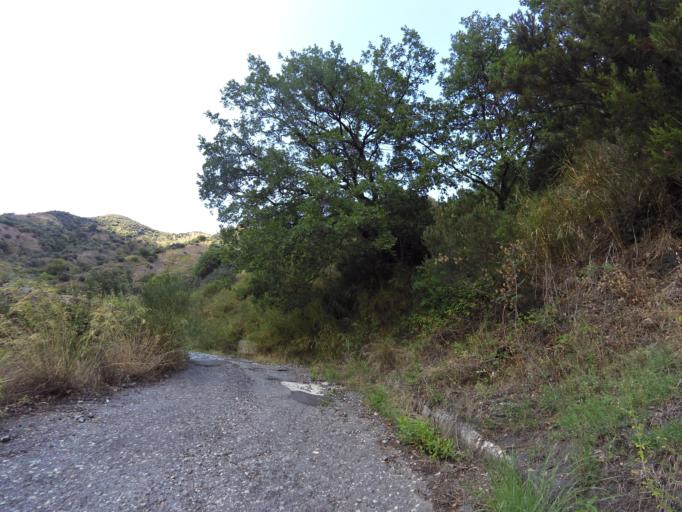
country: IT
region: Calabria
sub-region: Provincia di Reggio Calabria
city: Bivongi
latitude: 38.4915
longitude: 16.4555
